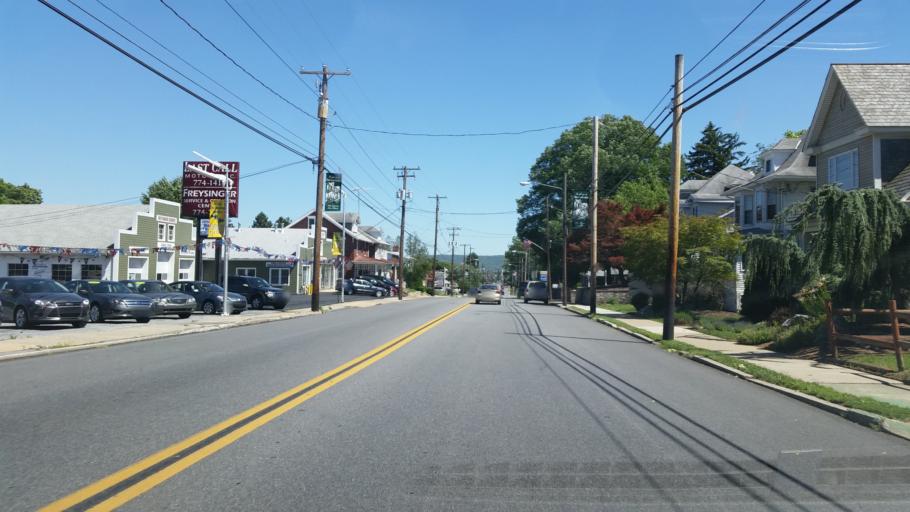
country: US
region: Pennsylvania
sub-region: Cumberland County
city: New Cumberland
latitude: 40.2363
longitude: -76.8786
